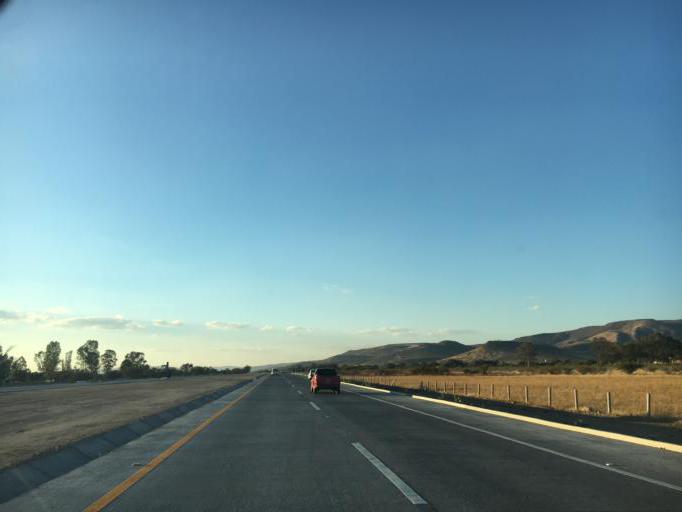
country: MX
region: Guanajuato
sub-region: Leon
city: Ladrilleras del Refugio
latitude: 21.0870
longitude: -101.5576
